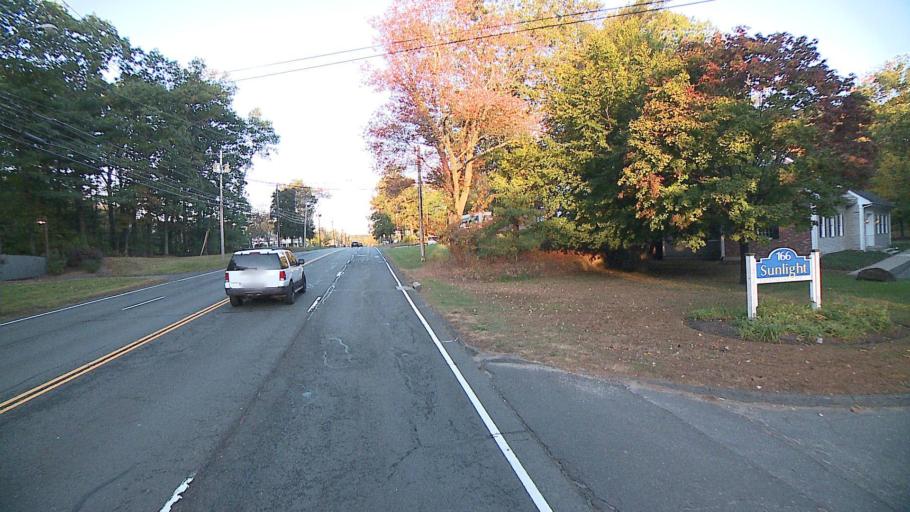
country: US
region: Connecticut
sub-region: Hartford County
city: Weatogue
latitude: 41.8115
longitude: -72.8451
